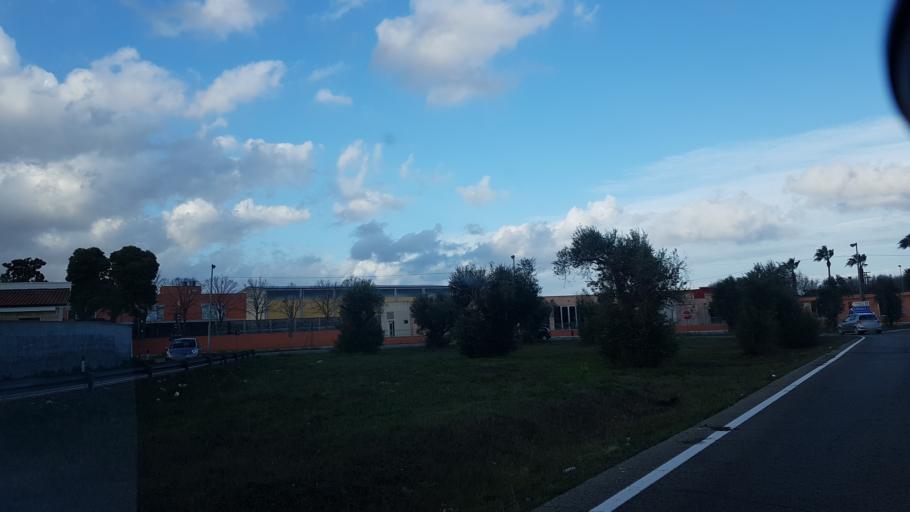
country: IT
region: Apulia
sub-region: Provincia di Brindisi
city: Torchiarolo
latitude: 40.4859
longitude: 18.0436
